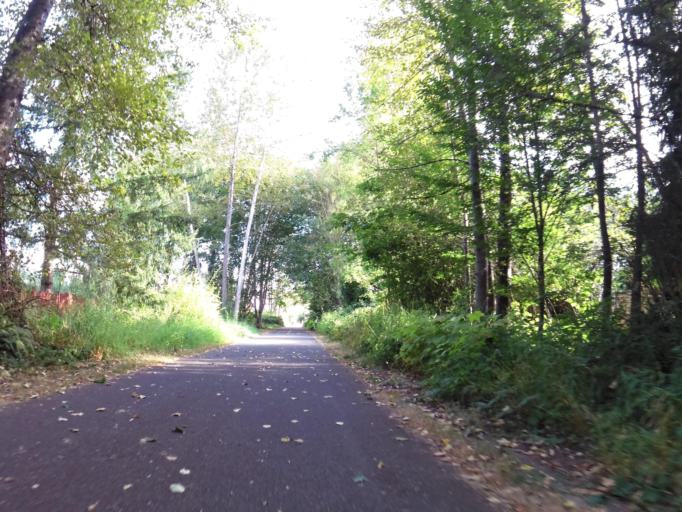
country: US
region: Washington
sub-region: Thurston County
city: Lacey
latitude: 47.0235
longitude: -122.8350
